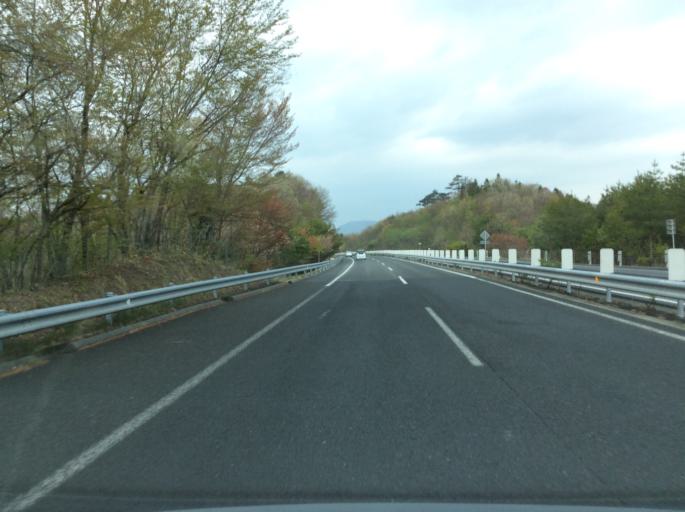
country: JP
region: Fukushima
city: Ishikawa
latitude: 37.2149
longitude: 140.6912
